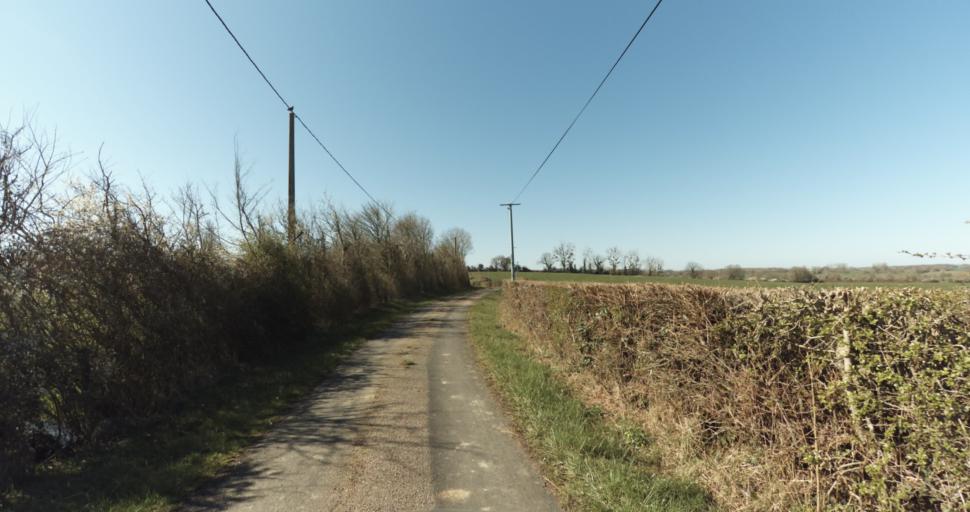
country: FR
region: Lower Normandy
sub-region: Departement de l'Orne
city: Trun
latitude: 48.9230
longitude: 0.0371
